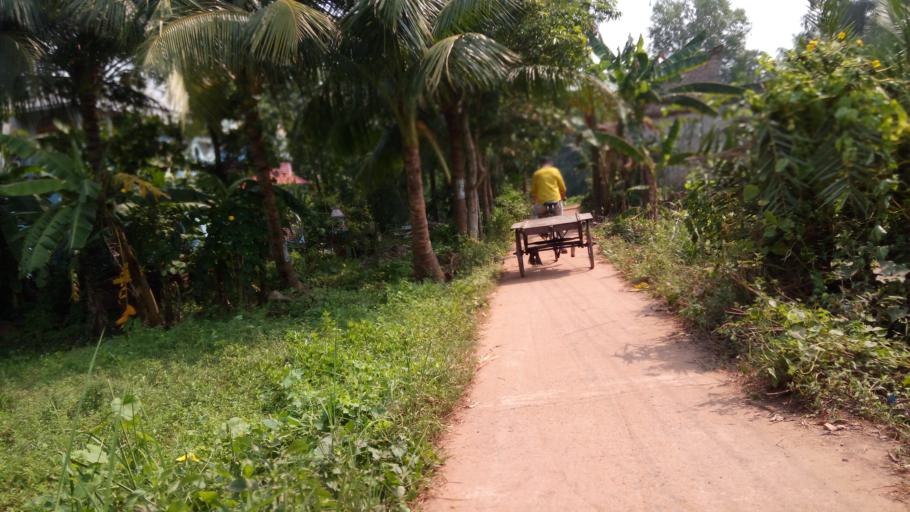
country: IN
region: West Bengal
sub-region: Purba Medinipur
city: Mahishadal
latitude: 22.1710
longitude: 87.9122
